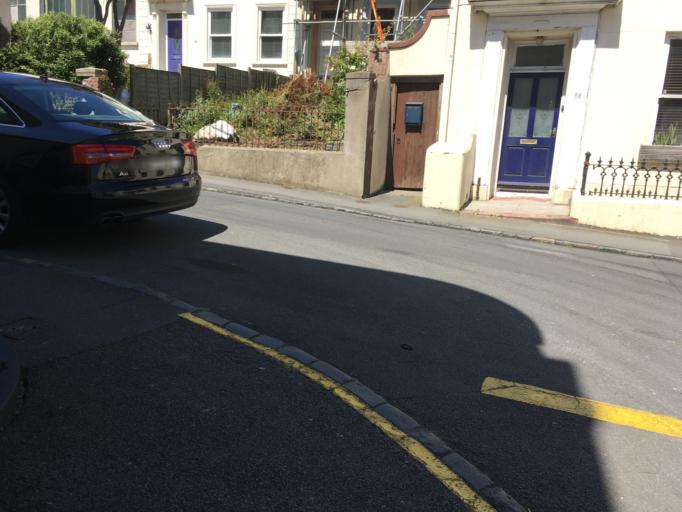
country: GG
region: St Peter Port
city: Saint Peter Port
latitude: 49.4540
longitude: -2.5447
